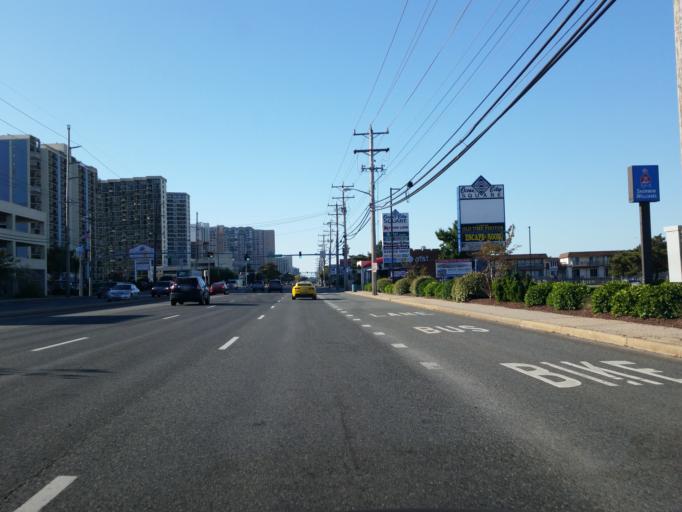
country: US
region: Maryland
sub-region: Worcester County
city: Ocean City
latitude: 38.4244
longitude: -75.0561
